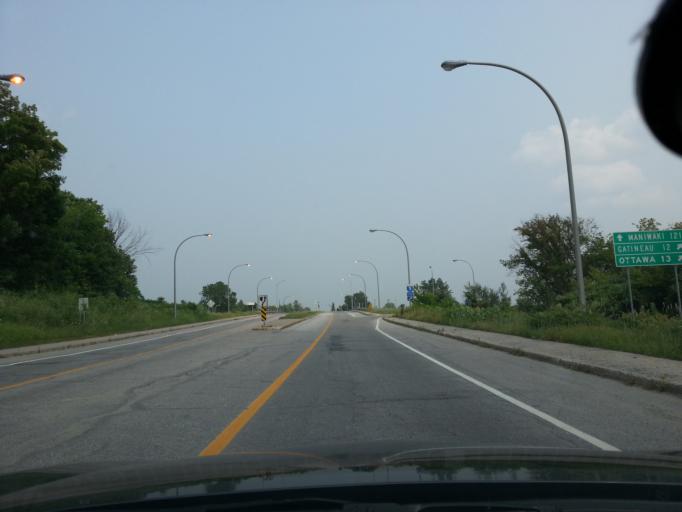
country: CA
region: Quebec
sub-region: Outaouais
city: Gatineau
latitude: 45.5033
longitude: -75.8020
